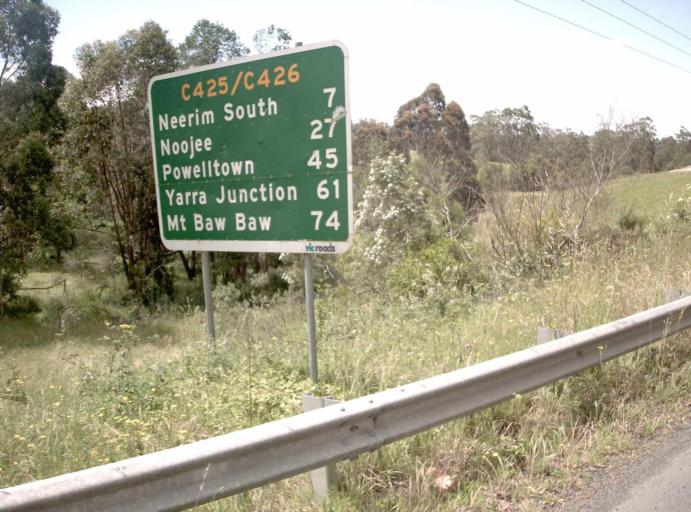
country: AU
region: Victoria
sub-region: Baw Baw
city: Warragul
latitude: -38.0652
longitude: 145.9264
